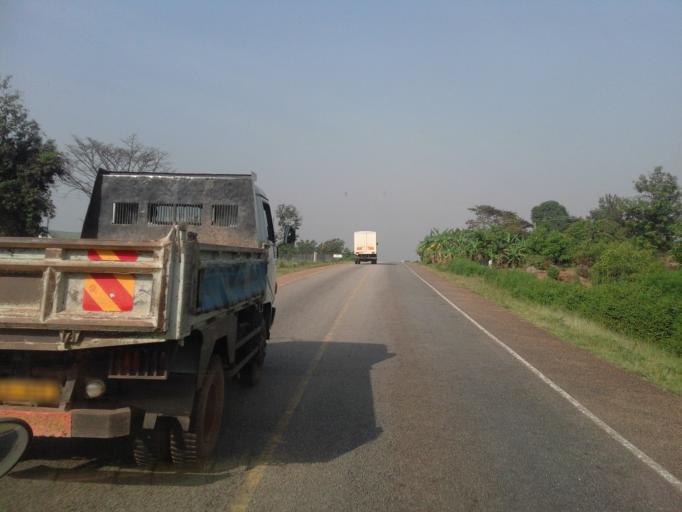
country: UG
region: Eastern Region
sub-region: Budaka District
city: Budaka
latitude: 1.0393
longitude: 34.0197
